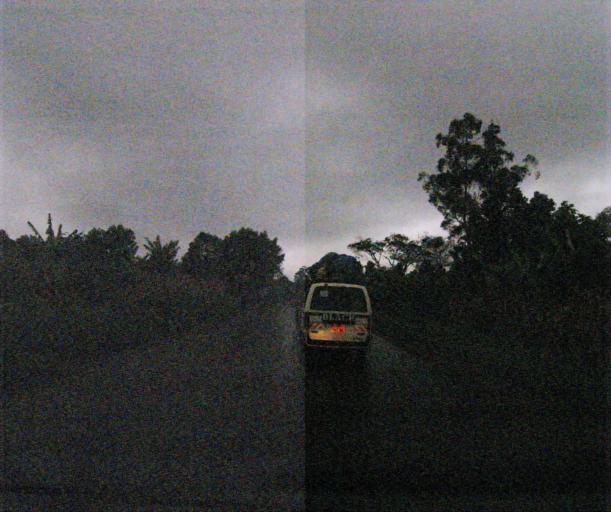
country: CM
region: West
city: Bansoa
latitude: 5.4737
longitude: 10.2904
